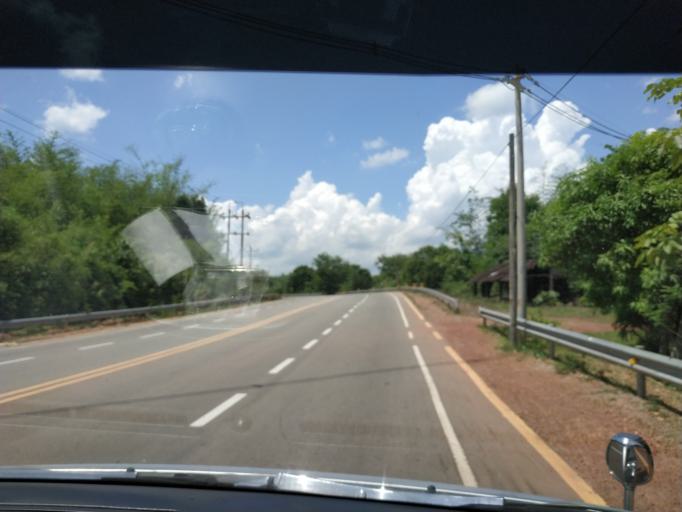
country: MM
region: Mon
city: Kyaikto
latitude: 17.3525
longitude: 97.0394
